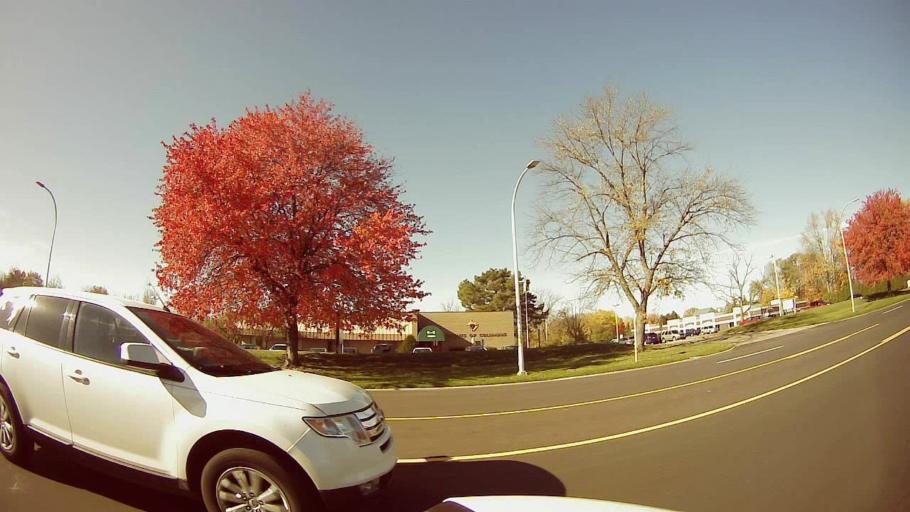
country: US
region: Michigan
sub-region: Oakland County
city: Farmington
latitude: 42.4327
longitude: -83.3752
